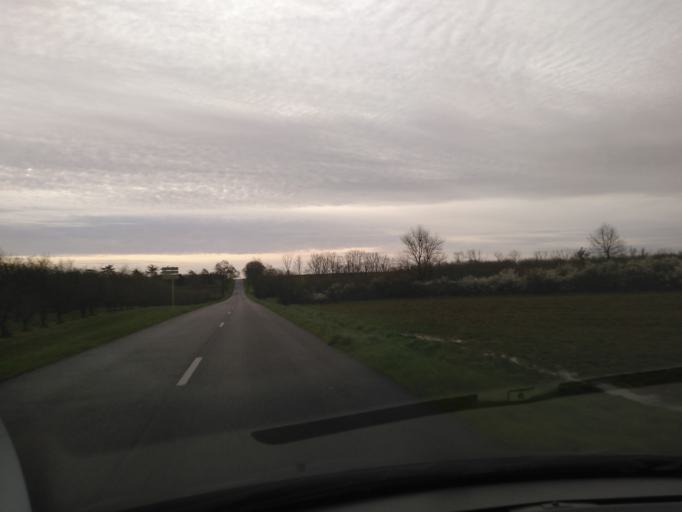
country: FR
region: Midi-Pyrenees
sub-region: Departement du Tarn-et-Garonne
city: Verdun-sur-Garonne
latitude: 43.8199
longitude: 1.1849
